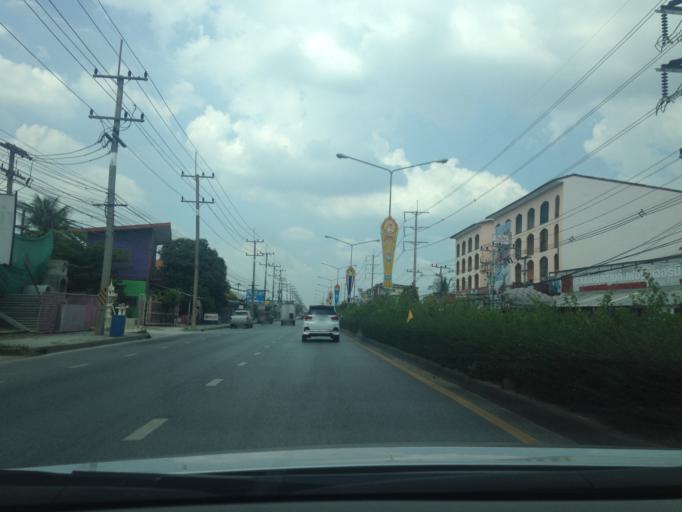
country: TH
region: Pathum Thani
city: Sam Khok
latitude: 14.0461
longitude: 100.5251
